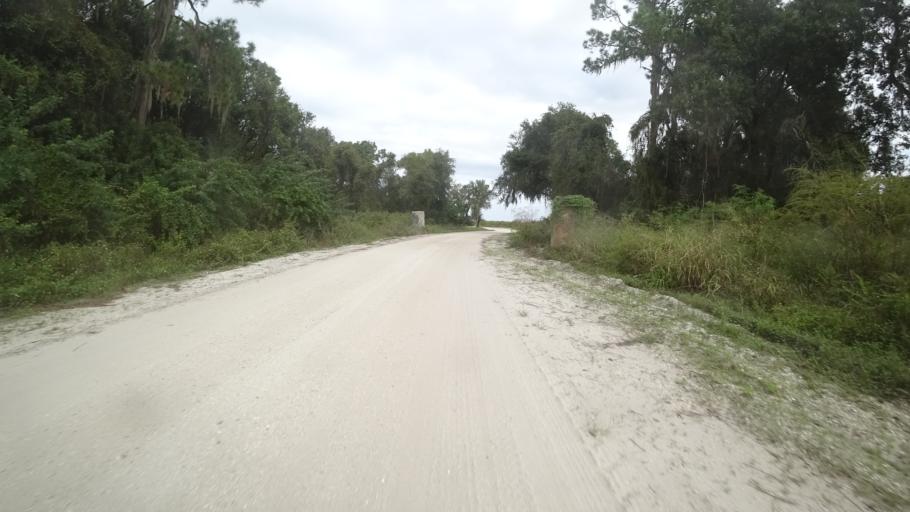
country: US
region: Florida
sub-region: Hillsborough County
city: Wimauma
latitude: 27.5726
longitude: -82.3126
